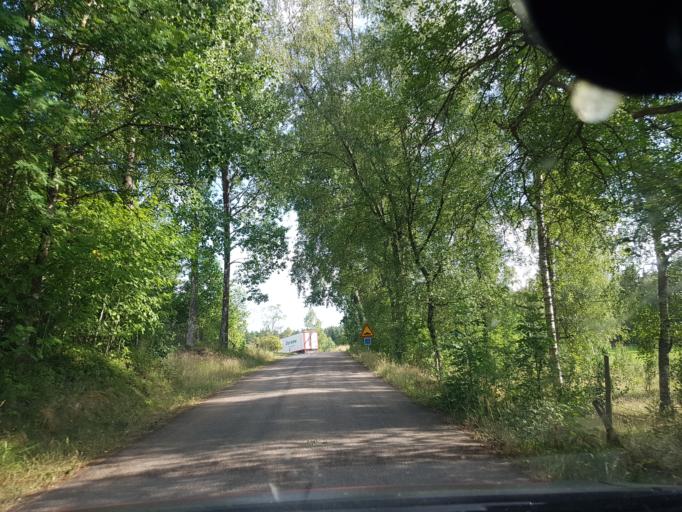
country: SE
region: Joenkoeping
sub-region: Gislaveds Kommun
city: Reftele
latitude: 57.2080
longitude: 13.5908
